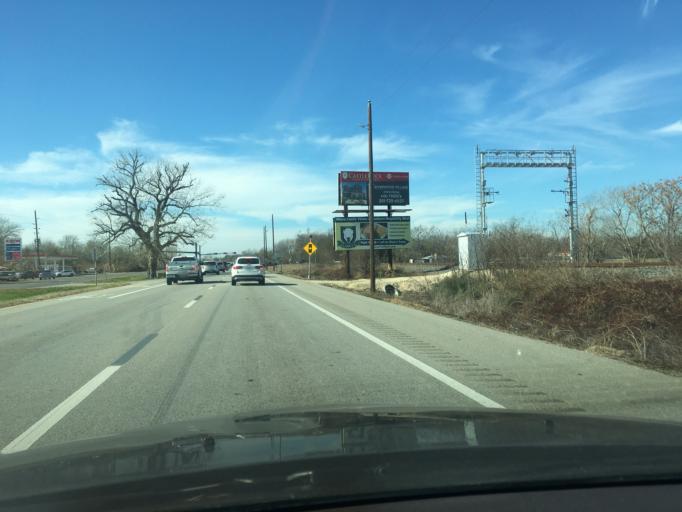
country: US
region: Texas
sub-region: Fort Bend County
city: Pecan Grove
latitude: 29.5969
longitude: -95.7316
